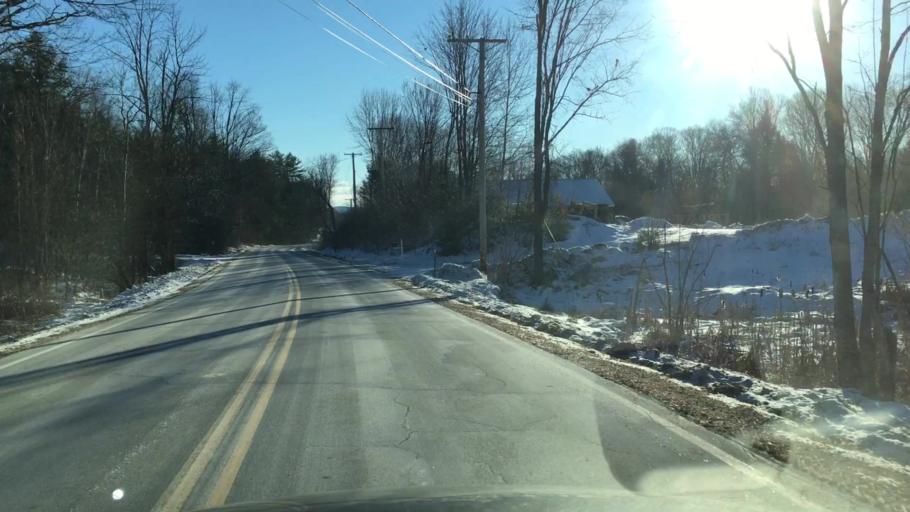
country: US
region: New Hampshire
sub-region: Grafton County
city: Woodsville
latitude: 44.2334
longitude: -72.0449
